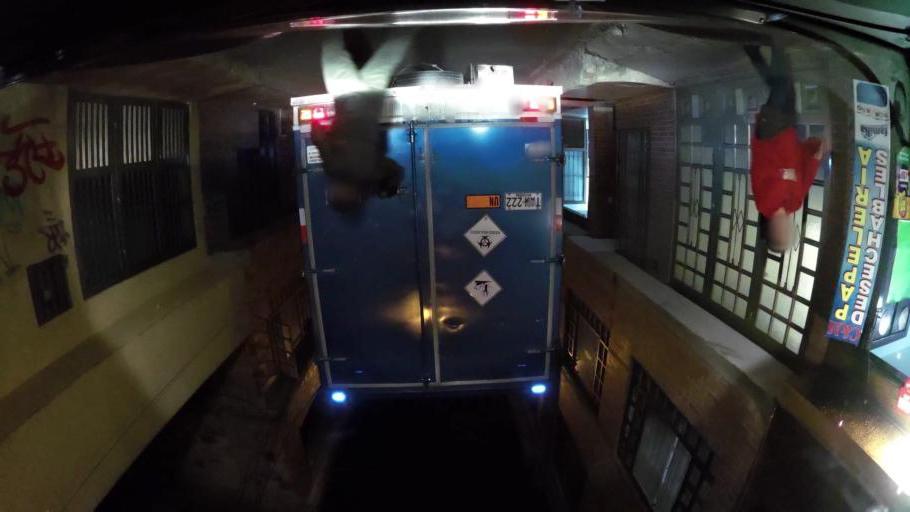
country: CO
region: Cundinamarca
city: Funza
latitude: 4.7150
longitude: -74.2224
